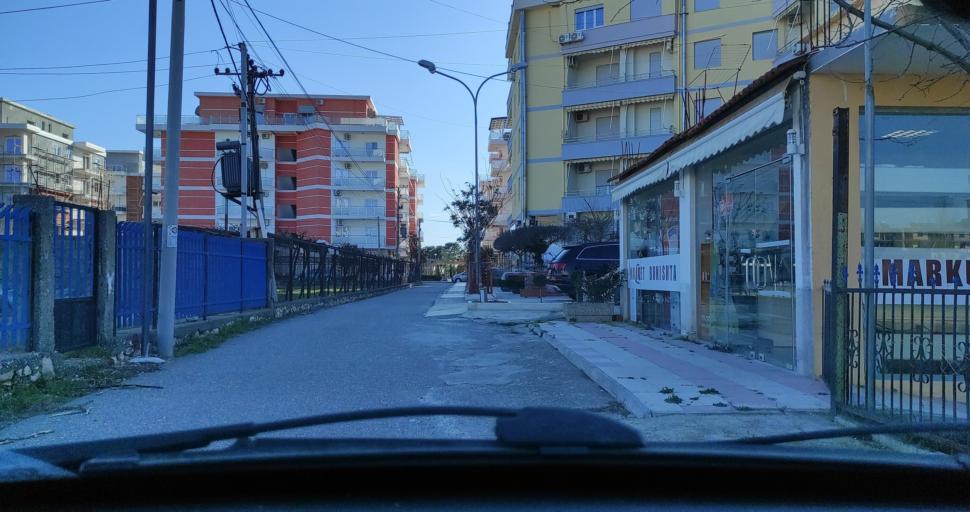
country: AL
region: Shkoder
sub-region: Rrethi i Shkodres
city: Velipoje
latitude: 41.8636
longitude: 19.4300
